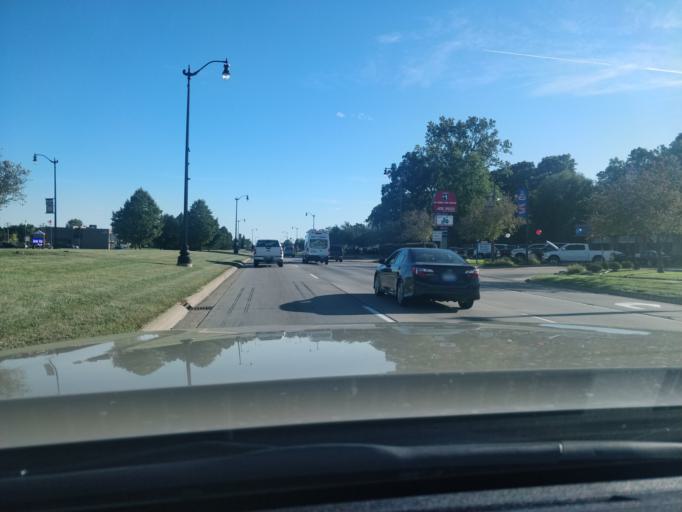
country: US
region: Michigan
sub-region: Wayne County
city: Taylor
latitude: 42.2165
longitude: -83.2690
